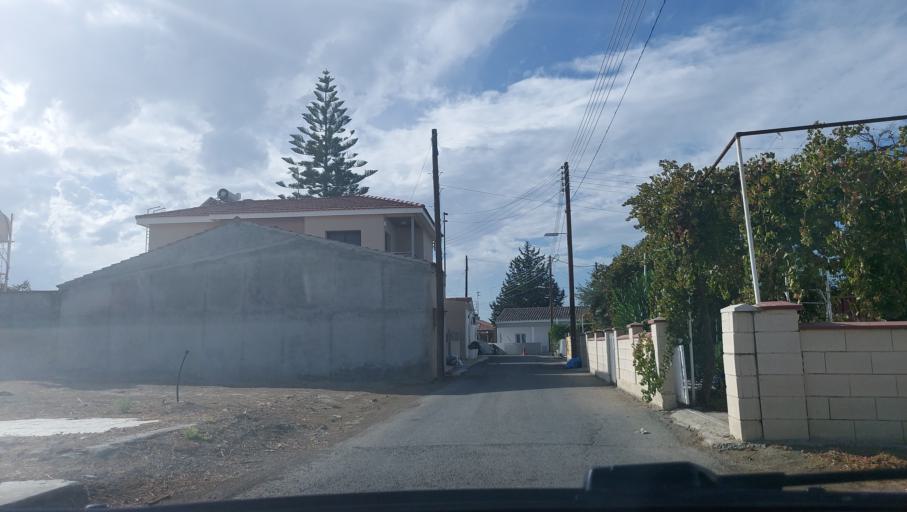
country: CY
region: Lefkosia
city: Pano Deftera
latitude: 35.0825
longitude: 33.2663
